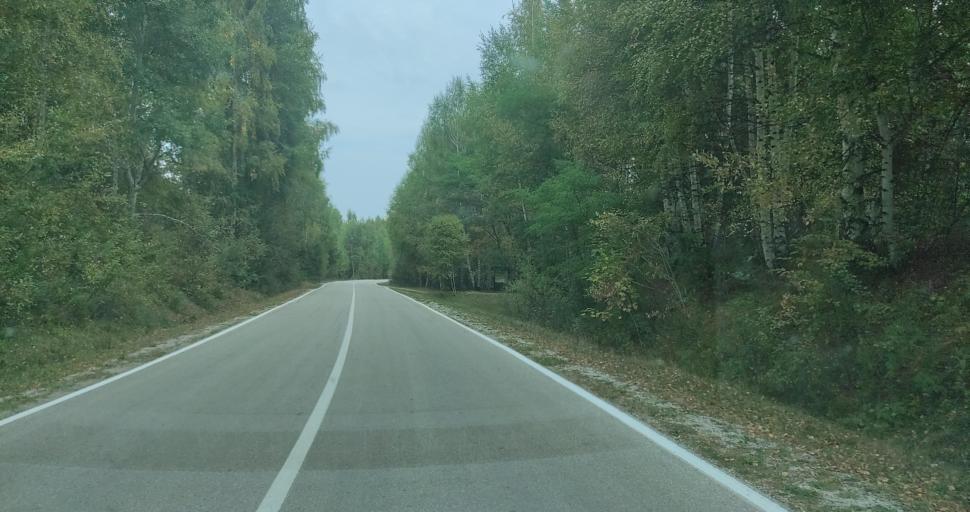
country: RS
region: Central Serbia
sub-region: Jablanicki Okrug
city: Crna Trava
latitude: 42.7215
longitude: 22.3347
